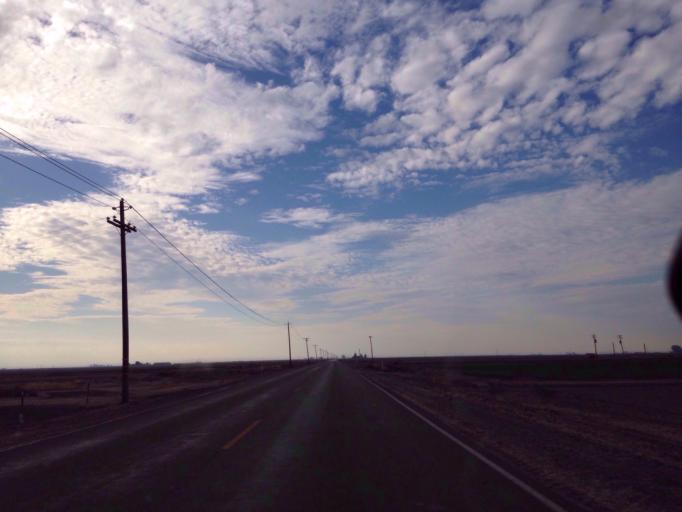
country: US
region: California
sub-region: Kern County
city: Buttonwillow
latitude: 35.4424
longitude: -119.5008
